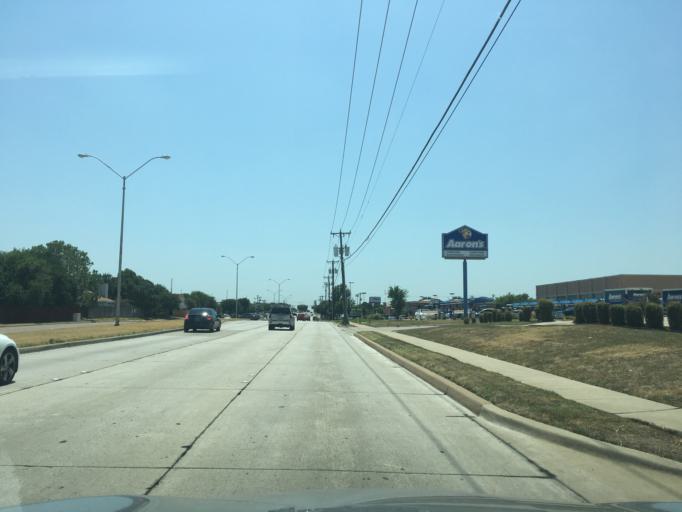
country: US
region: Texas
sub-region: Tarrant County
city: Edgecliff Village
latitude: 32.6392
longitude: -97.3698
